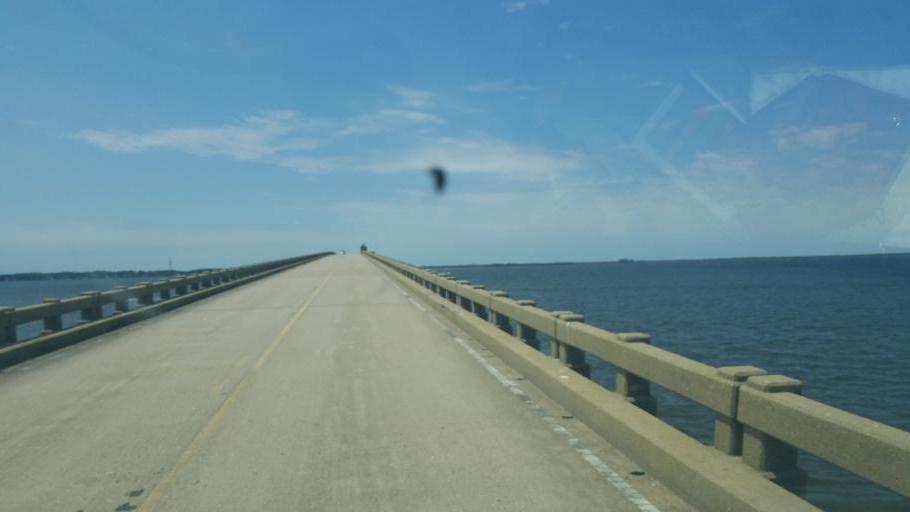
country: US
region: North Carolina
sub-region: Dare County
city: Manteo
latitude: 35.9199
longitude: -75.7453
